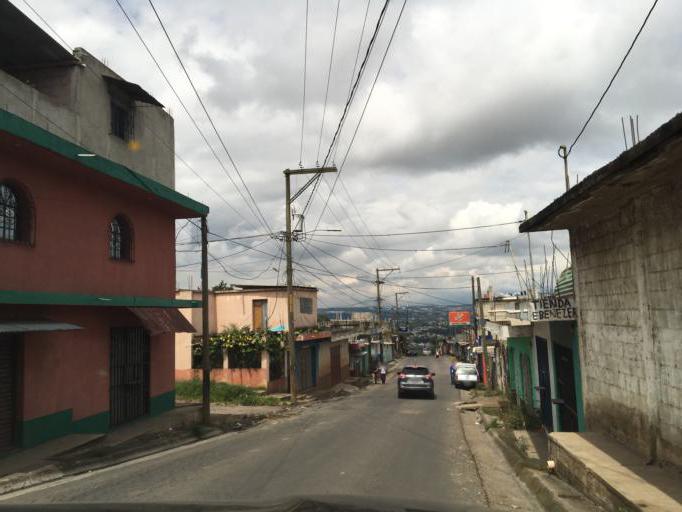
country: GT
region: Guatemala
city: Villa Nueva
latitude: 14.5017
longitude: -90.5909
